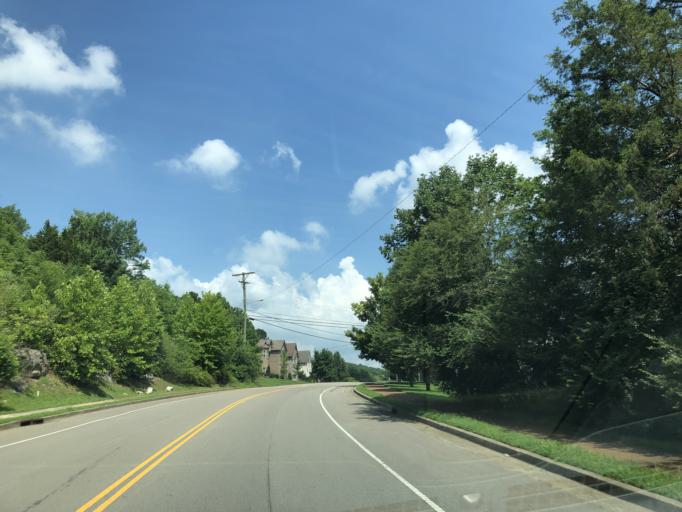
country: US
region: Tennessee
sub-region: Williamson County
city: Nolensville
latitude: 36.0124
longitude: -86.6972
